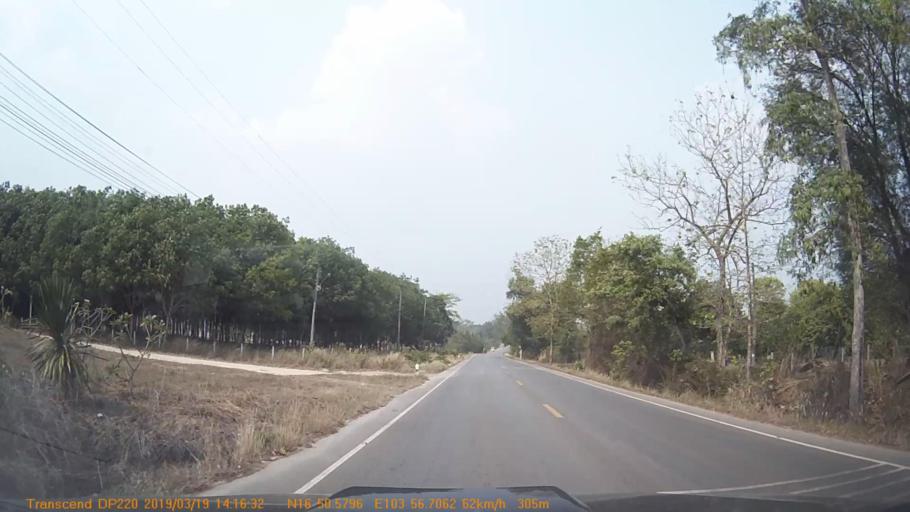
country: TH
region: Kalasin
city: Na Khu
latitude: 16.8433
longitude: 103.9452
